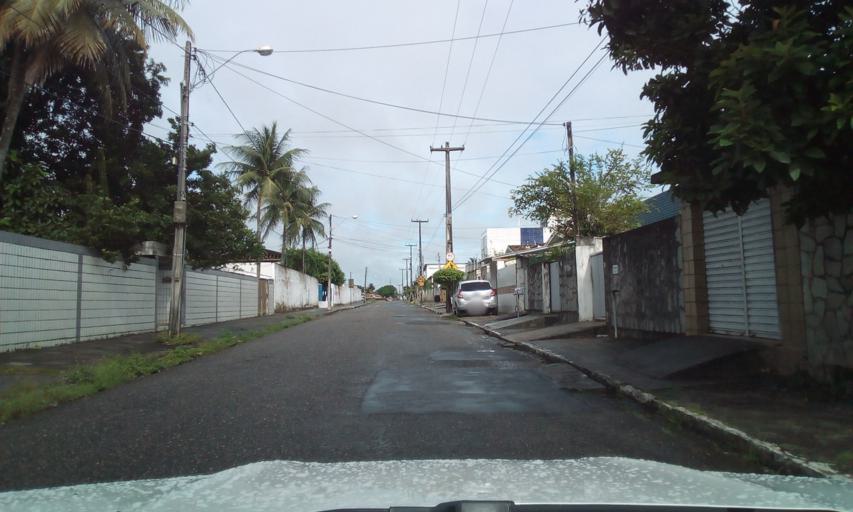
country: BR
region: Paraiba
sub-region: Joao Pessoa
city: Joao Pessoa
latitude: -7.1483
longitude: -34.8797
